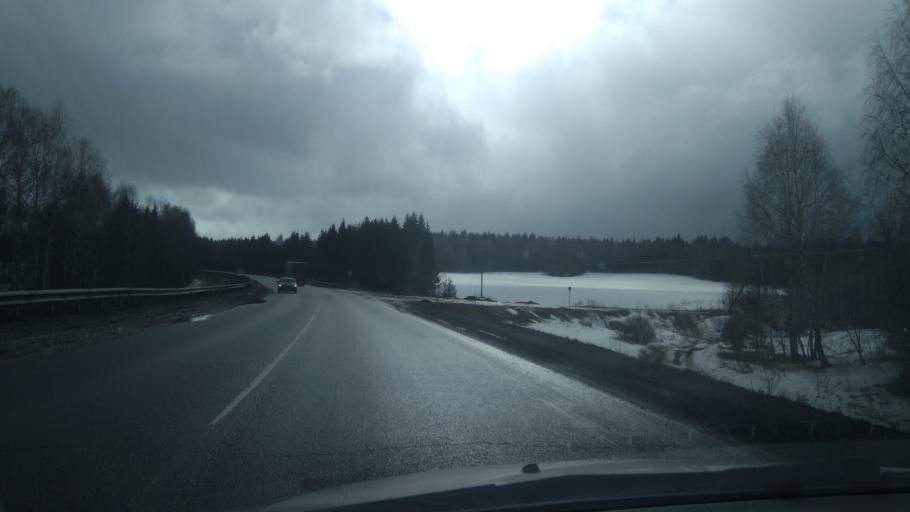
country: RU
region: Perm
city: Kukushtan
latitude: 57.4867
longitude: 56.6691
